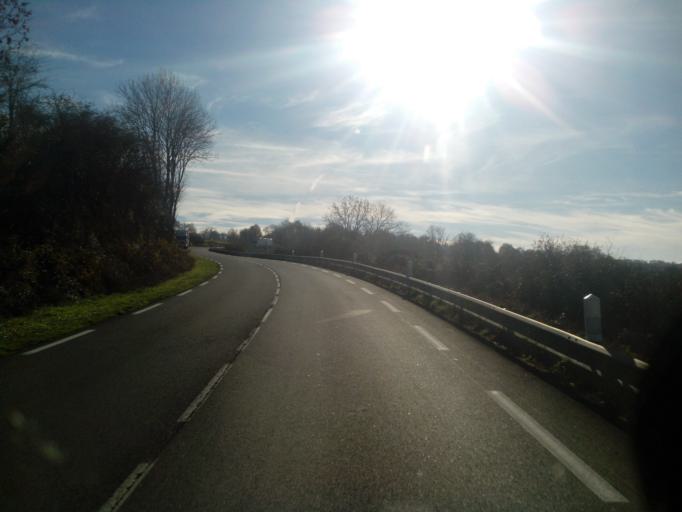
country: FR
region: Limousin
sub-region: Departement de la Haute-Vienne
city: Peyrat-de-Bellac
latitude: 46.1609
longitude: 0.9595
